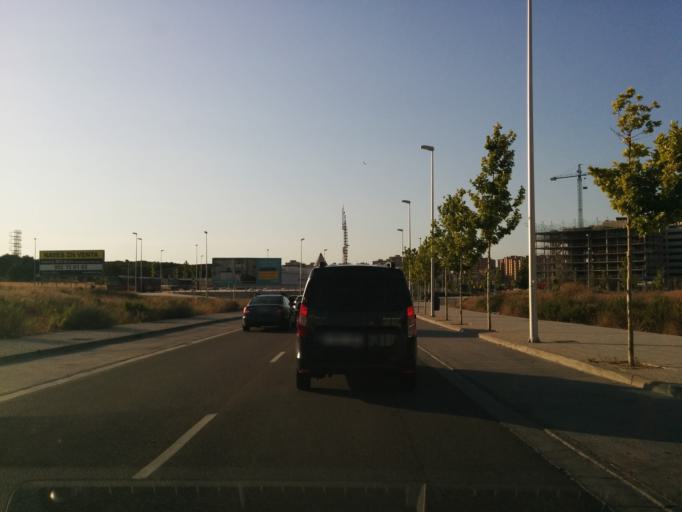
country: ES
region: Aragon
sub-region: Provincia de Zaragoza
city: Zaragoza
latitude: 41.6168
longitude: -0.8757
